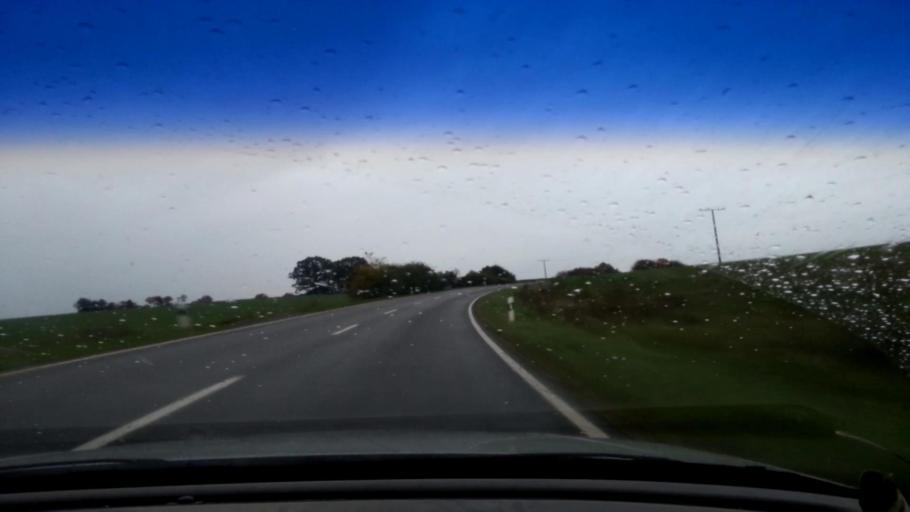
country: DE
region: Bavaria
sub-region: Upper Franconia
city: Burgebrach
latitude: 49.8559
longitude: 10.7251
